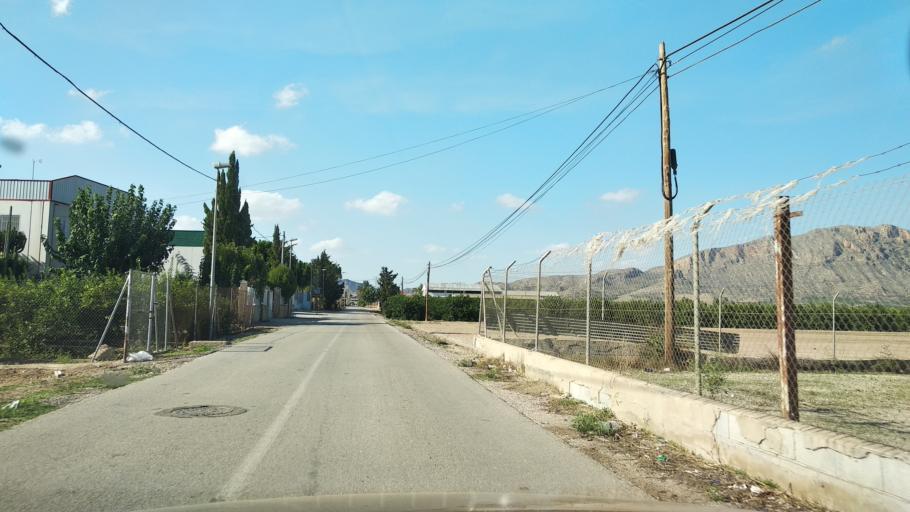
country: ES
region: Murcia
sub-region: Murcia
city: Santomera
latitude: 38.0509
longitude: -1.0404
